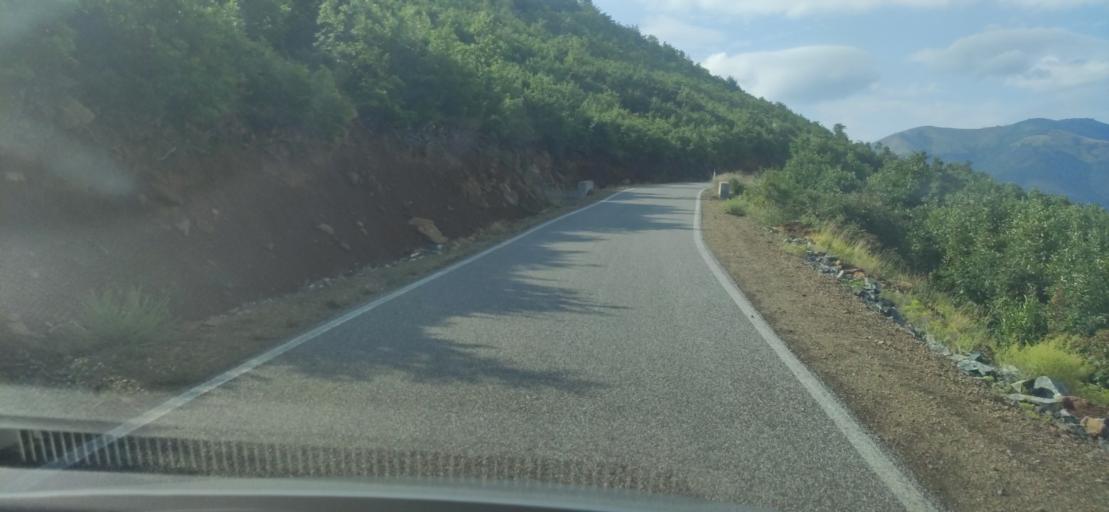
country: AL
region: Shkoder
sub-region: Rrethi i Pukes
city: Iballe
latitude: 42.1702
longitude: 20.0029
